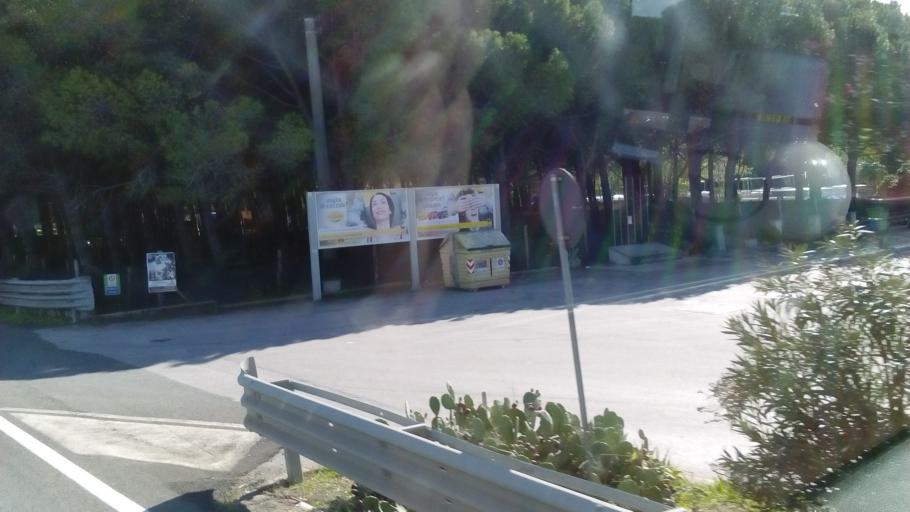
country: IT
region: Tuscany
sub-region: Provincia di Grosseto
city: Fonteblanda
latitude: 42.5468
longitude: 11.1759
